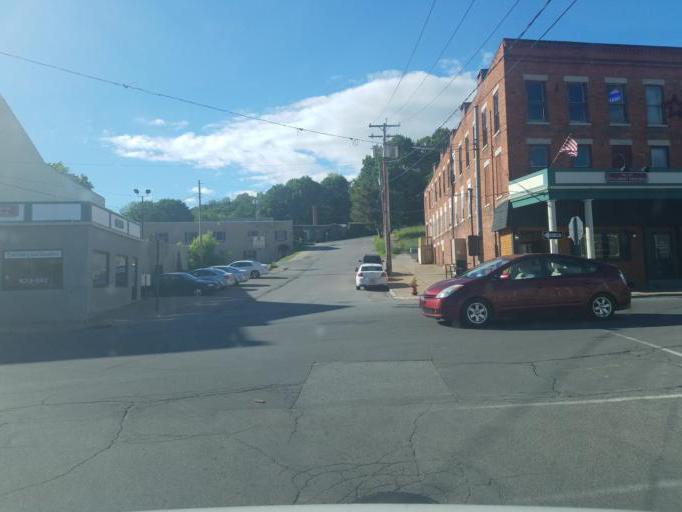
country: US
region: New York
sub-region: Herkimer County
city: Little Falls
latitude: 43.0435
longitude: -74.8585
